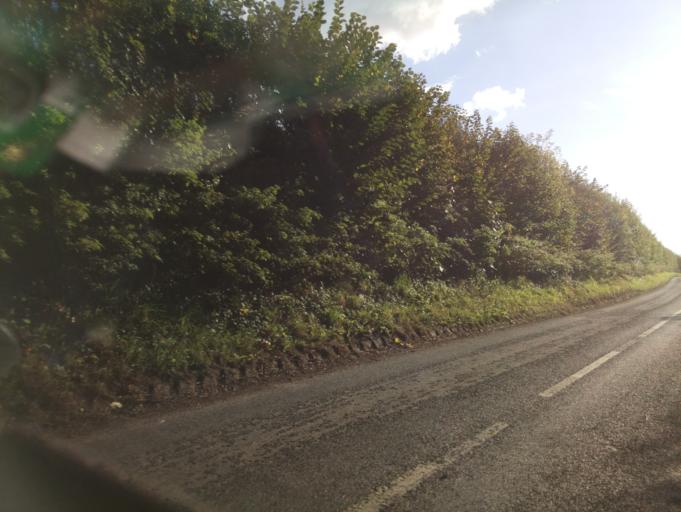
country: GB
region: England
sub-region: Herefordshire
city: Clifford
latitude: 52.1092
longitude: -3.0974
